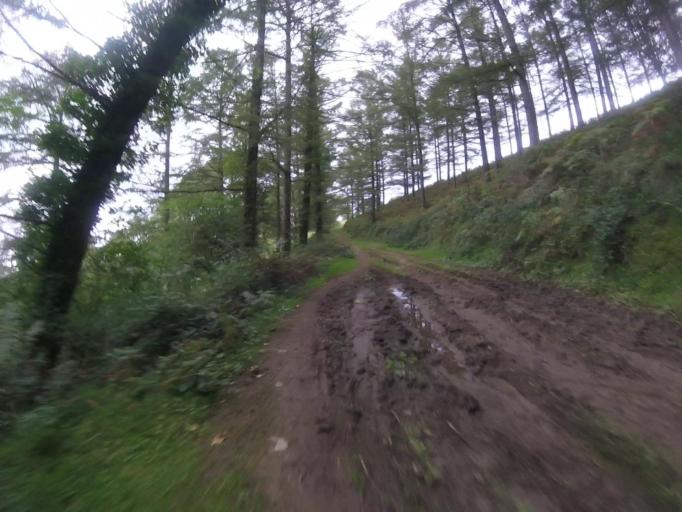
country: ES
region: Basque Country
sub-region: Provincia de Guipuzcoa
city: Irun
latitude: 43.2613
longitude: -1.8293
